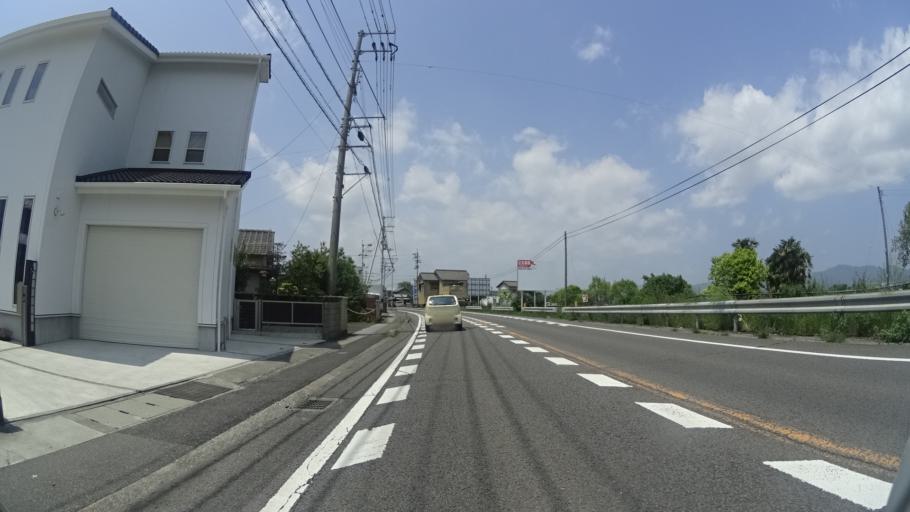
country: JP
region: Tokushima
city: Ishii
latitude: 34.0673
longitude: 134.4249
